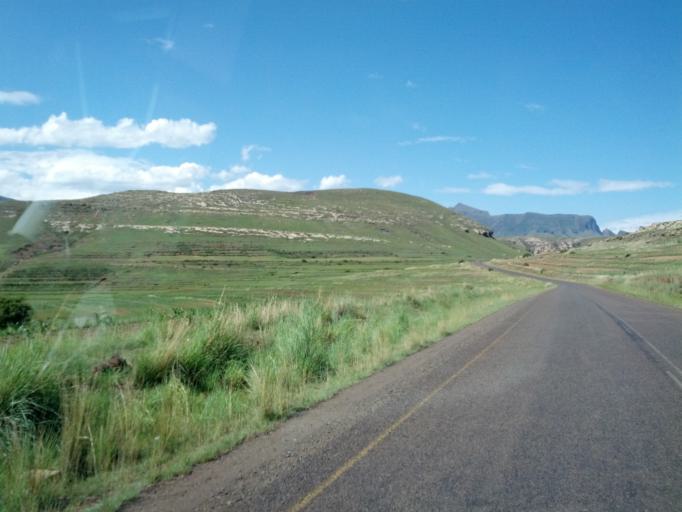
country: LS
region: Qacha's Nek
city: Qacha's Nek
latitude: -30.0533
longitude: 28.4878
